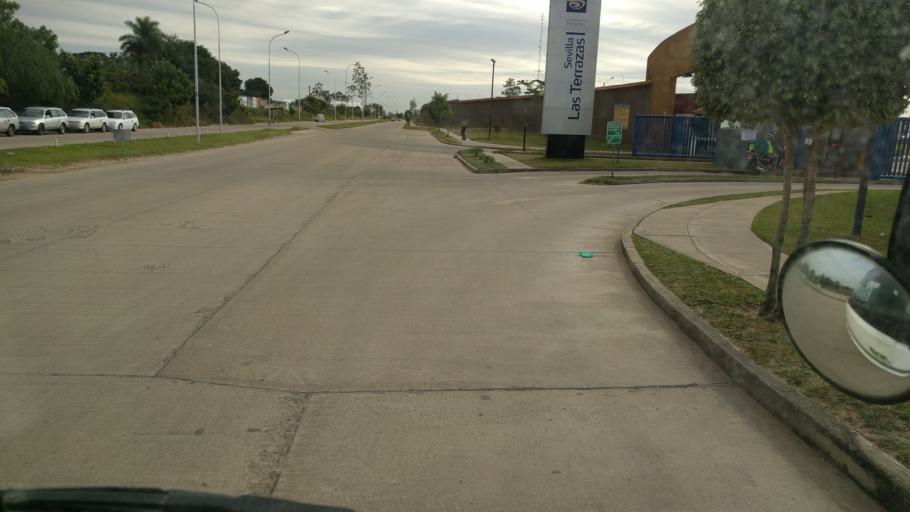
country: BO
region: Santa Cruz
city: Santa Cruz de la Sierra
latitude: -17.6831
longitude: -63.1533
